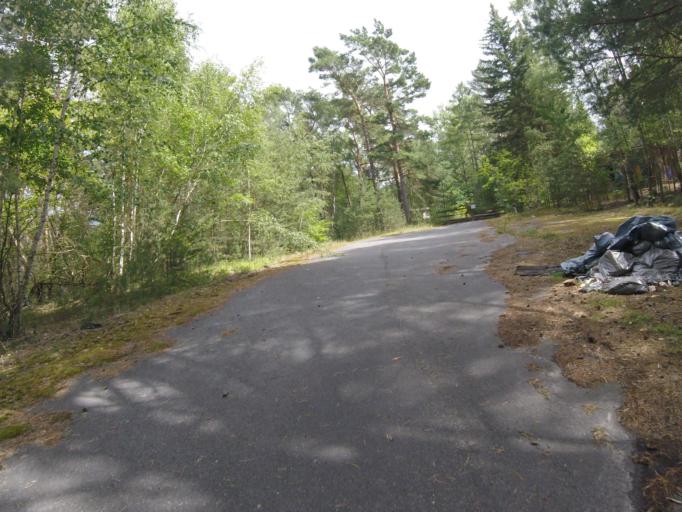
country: DE
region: Brandenburg
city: Wildau
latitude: 52.3292
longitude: 13.6632
